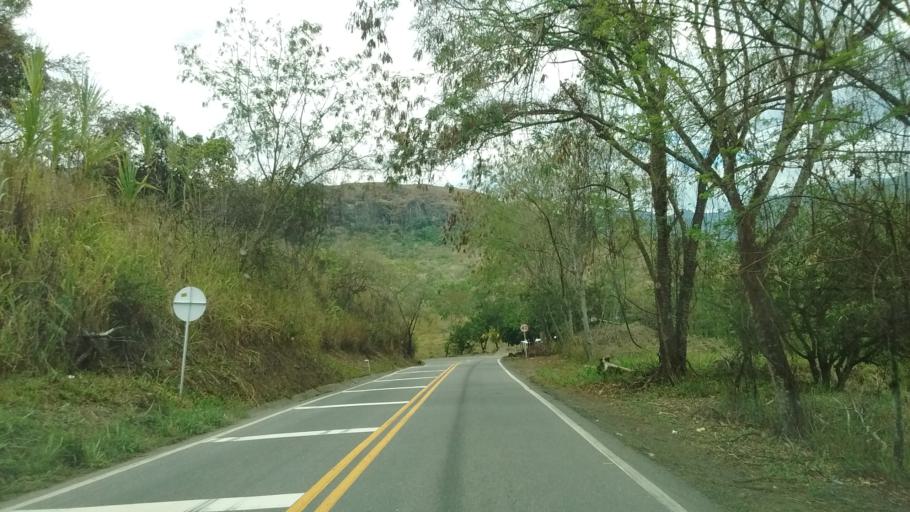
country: CO
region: Cauca
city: La Sierra
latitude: 2.2035
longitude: -76.8132
